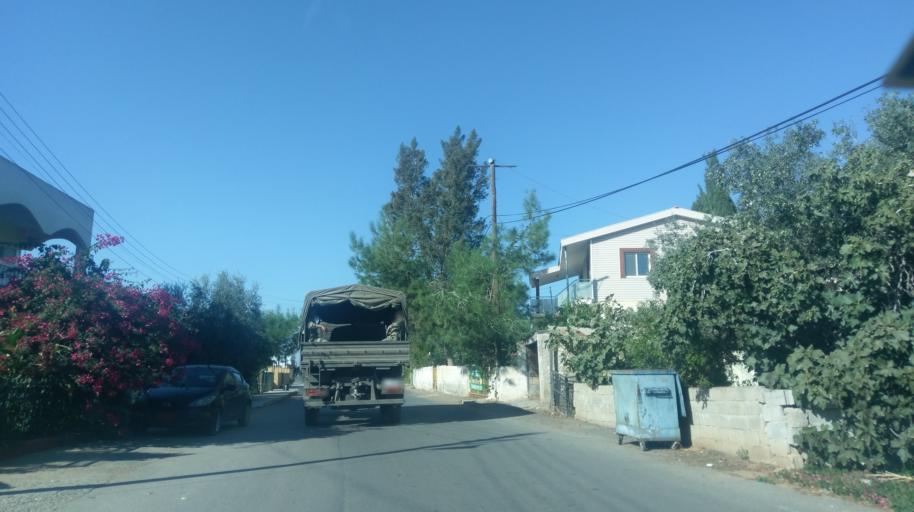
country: CY
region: Ammochostos
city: Famagusta
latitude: 35.0998
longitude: 33.9494
